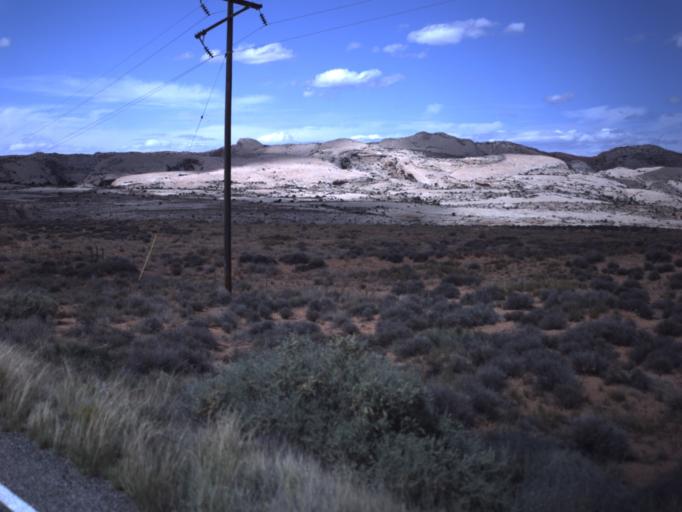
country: US
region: Utah
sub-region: San Juan County
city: Blanding
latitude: 37.2641
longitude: -109.6437
